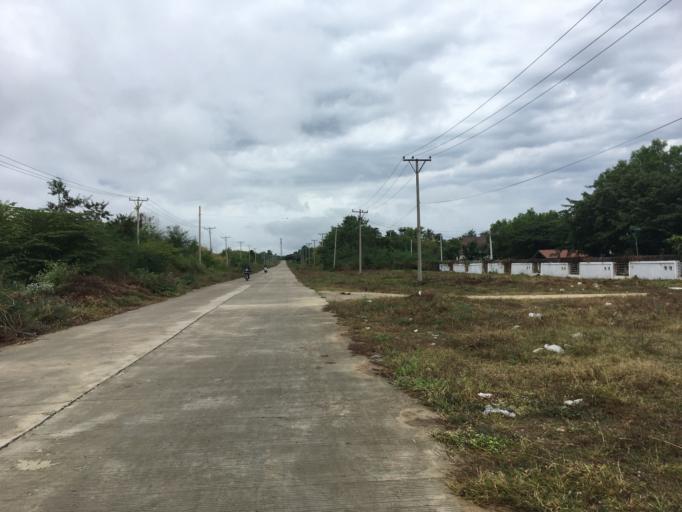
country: MM
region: Mandalay
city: Nay Pyi Taw
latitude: 19.6994
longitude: 96.1182
